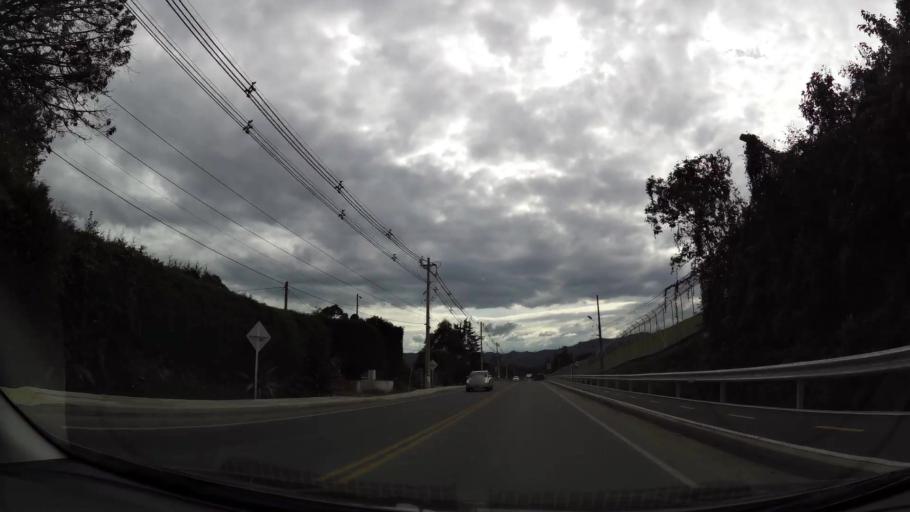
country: CO
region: Antioquia
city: Rionegro
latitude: 6.1480
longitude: -75.4209
